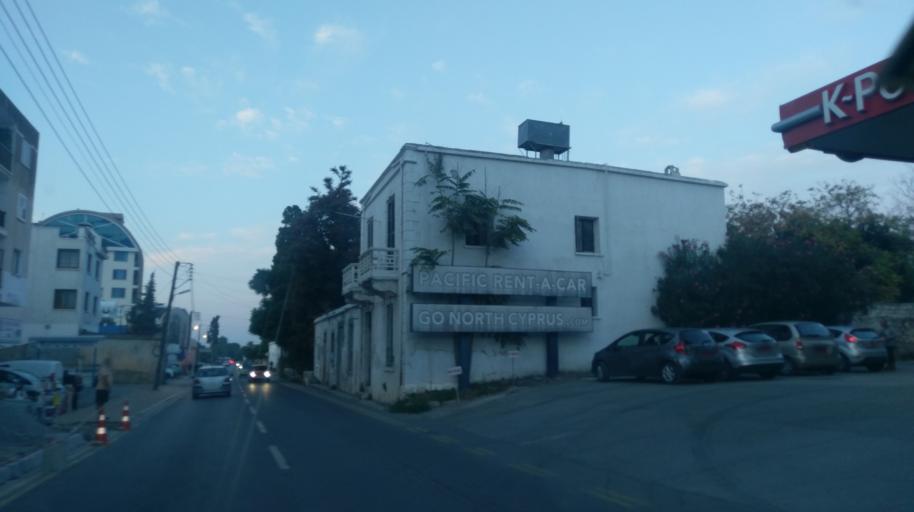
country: CY
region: Keryneia
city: Kyrenia
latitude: 35.3363
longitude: 33.3200
